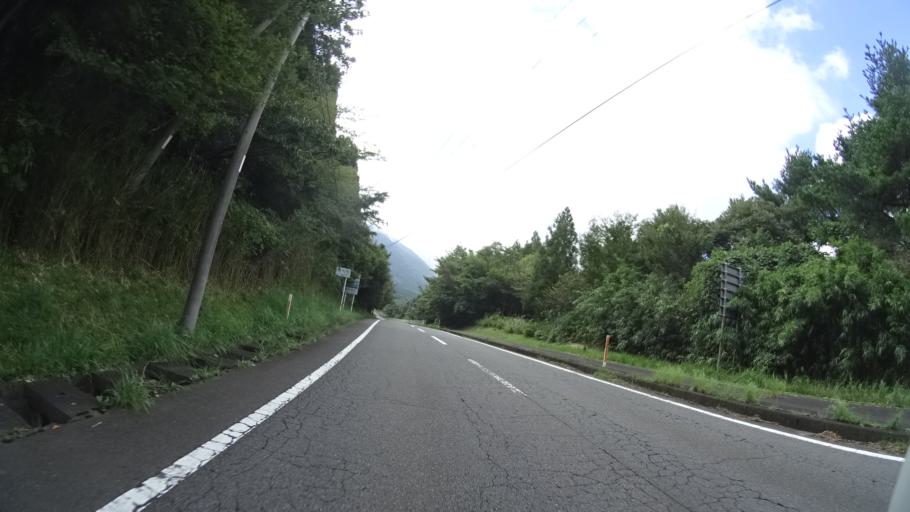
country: JP
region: Oita
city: Beppu
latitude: 33.3211
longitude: 131.4141
